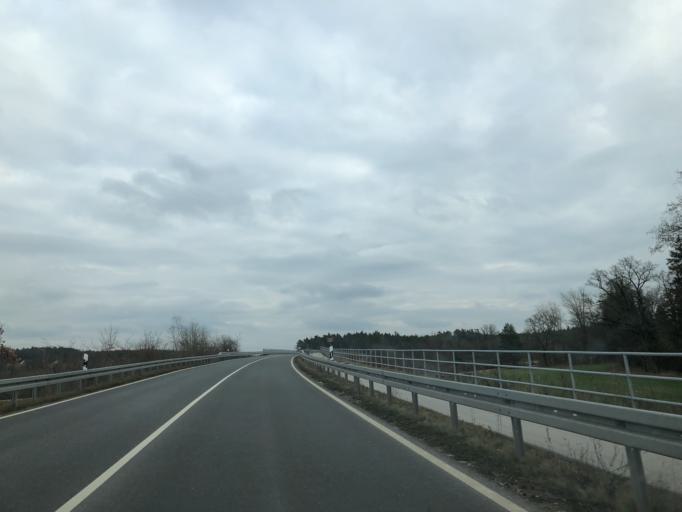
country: DE
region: Bavaria
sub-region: Regierungsbezirk Mittelfranken
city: Rednitzhembach
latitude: 49.2999
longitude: 11.0979
